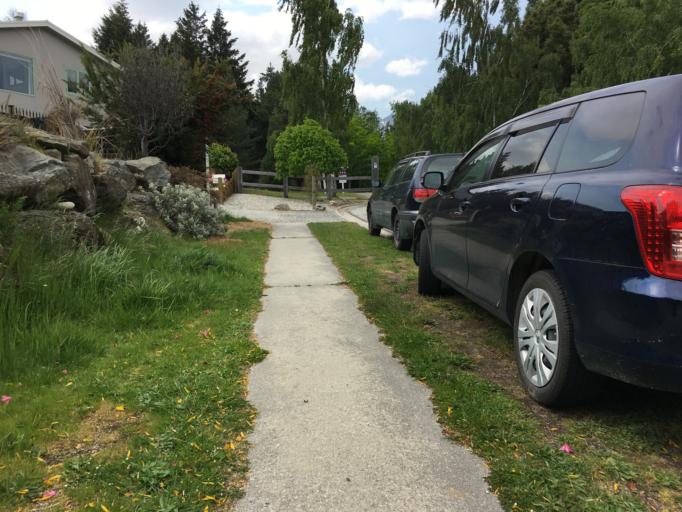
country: NZ
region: Otago
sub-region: Queenstown-Lakes District
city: Queenstown
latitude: -45.0462
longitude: 168.6883
